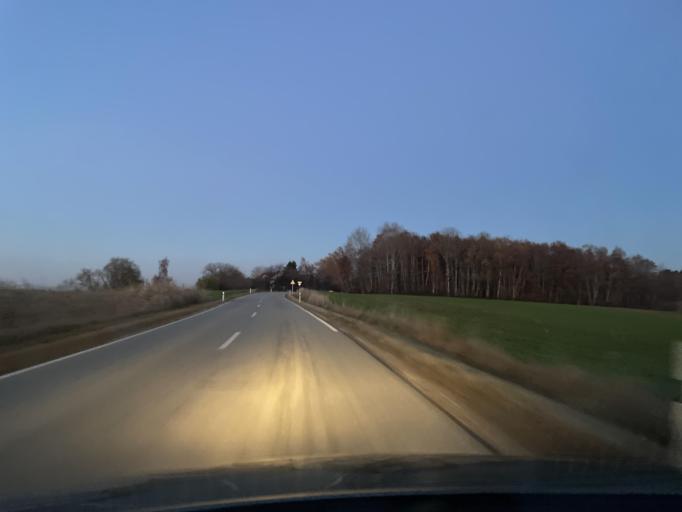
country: DE
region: Bavaria
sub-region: Lower Bavaria
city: Wittibreut
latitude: 48.3217
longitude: 12.9739
